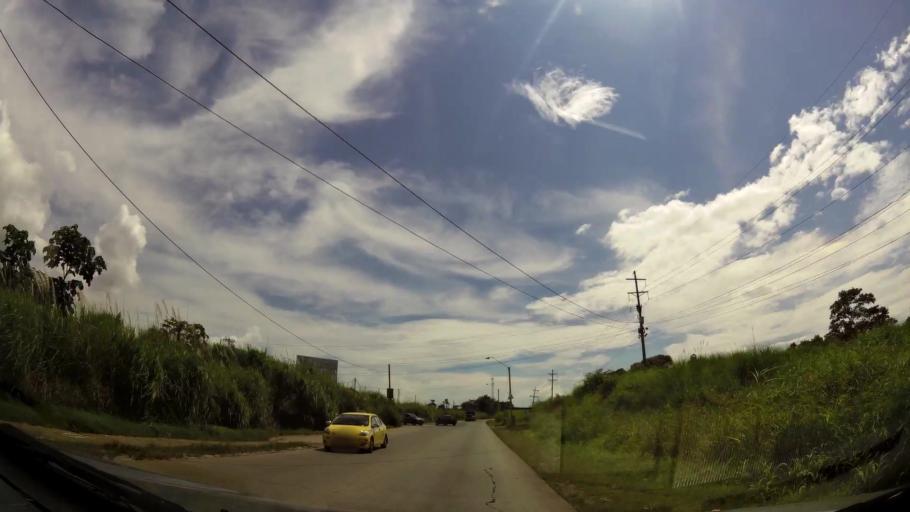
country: PA
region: Panama
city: San Vicente de Bique
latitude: 8.9174
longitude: -79.6935
